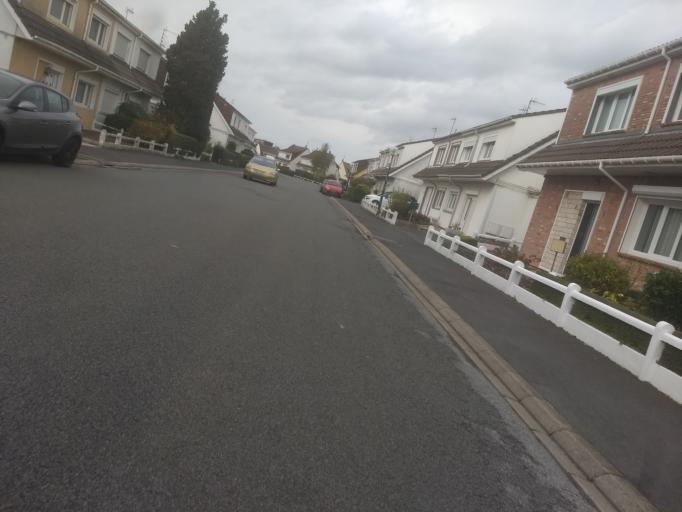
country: FR
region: Nord-Pas-de-Calais
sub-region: Departement du Pas-de-Calais
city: Agny
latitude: 50.2663
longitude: 2.7733
